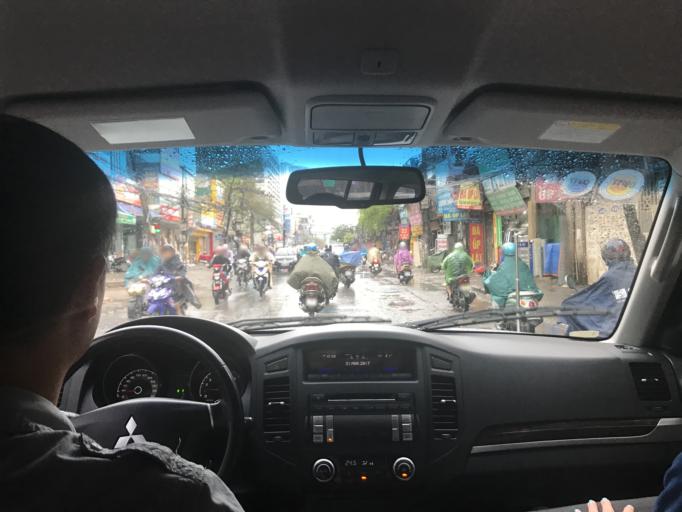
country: VN
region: Ha Noi
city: Dong Da
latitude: 21.0019
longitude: 105.8248
